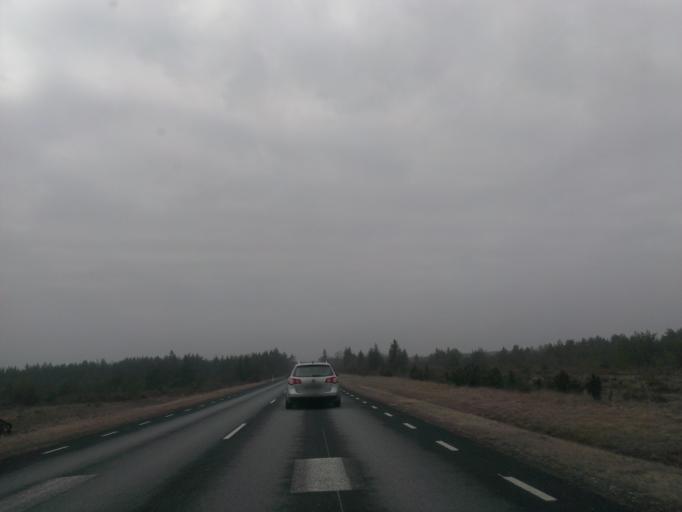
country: EE
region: Saare
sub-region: Orissaare vald
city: Orissaare
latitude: 58.5882
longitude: 23.3410
